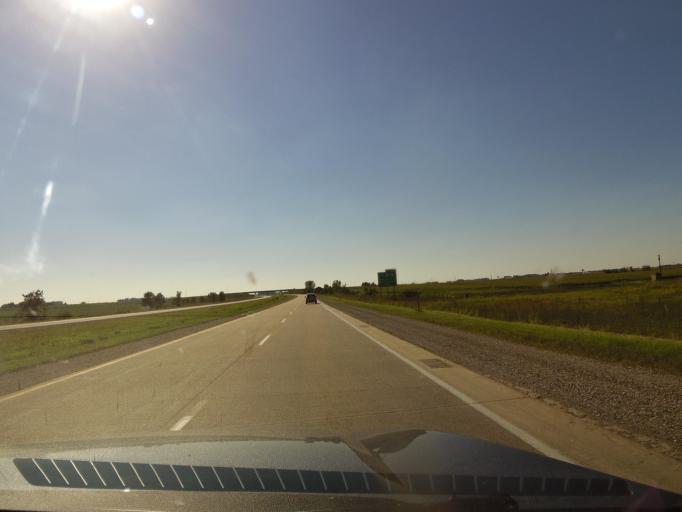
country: US
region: Iowa
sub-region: Cerro Gordo County
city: Clear Lake
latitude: 43.1055
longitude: -93.3108
